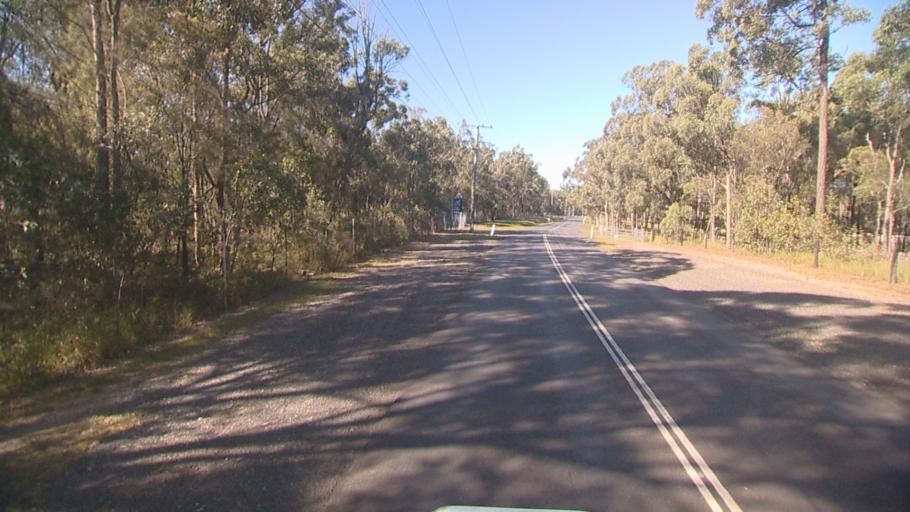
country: AU
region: Queensland
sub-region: Logan
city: Rochedale South
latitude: -27.5912
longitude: 153.1518
